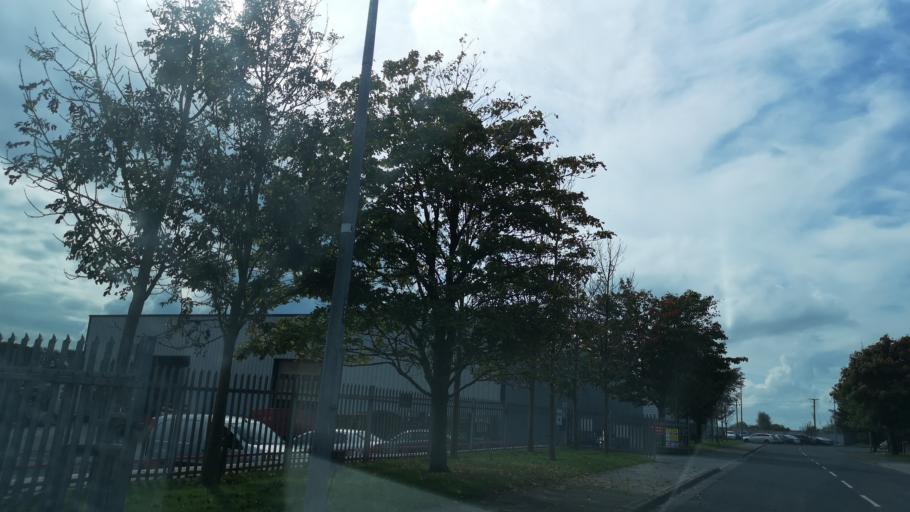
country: IE
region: Connaught
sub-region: County Galway
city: Athenry
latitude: 53.3005
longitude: -8.7524
